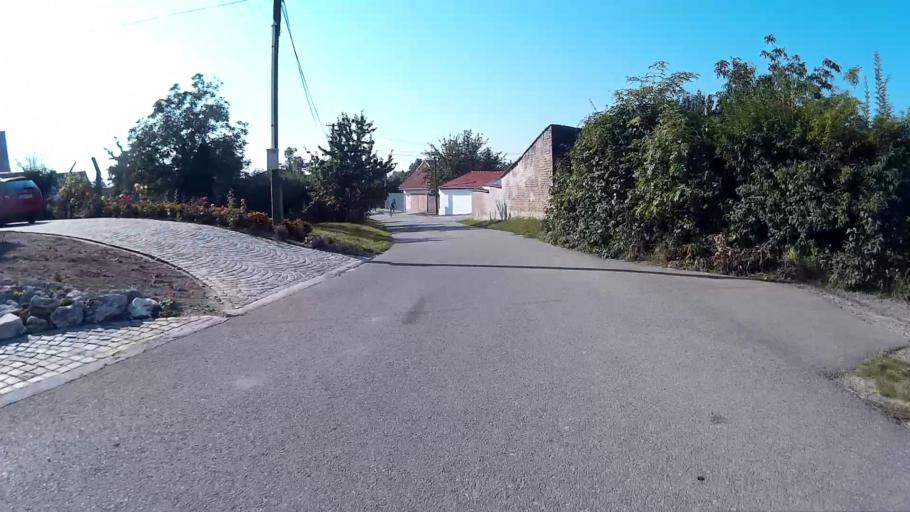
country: CZ
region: South Moravian
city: Vranovice
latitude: 48.9311
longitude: 16.5758
